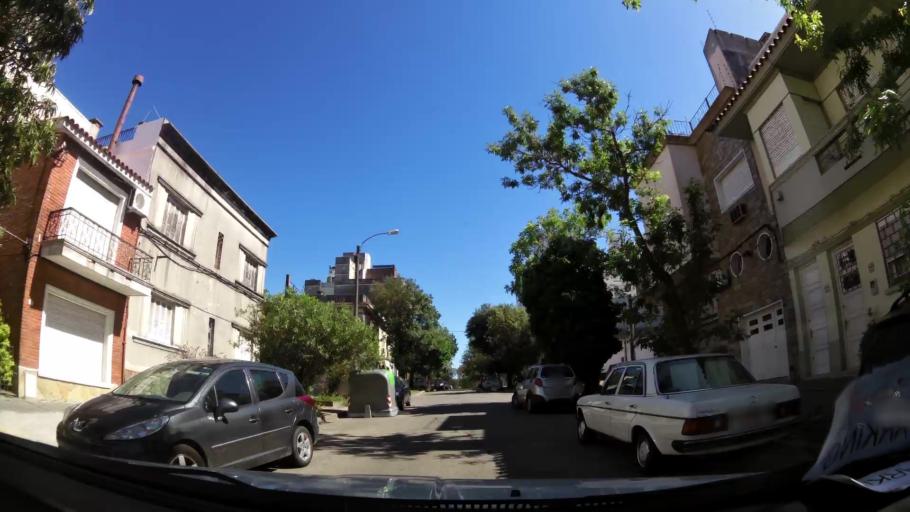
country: UY
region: Montevideo
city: Montevideo
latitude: -34.9161
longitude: -56.1640
